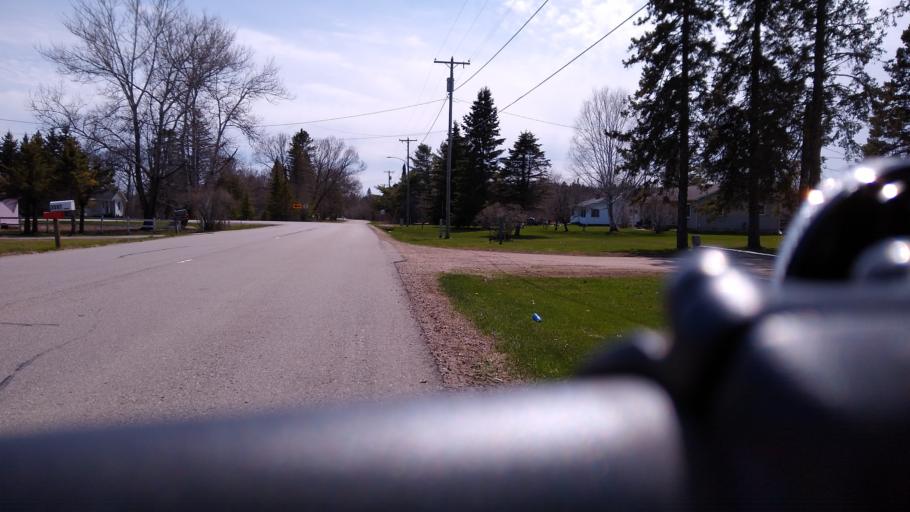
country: US
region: Michigan
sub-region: Delta County
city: Escanaba
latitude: 45.6778
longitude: -87.1465
